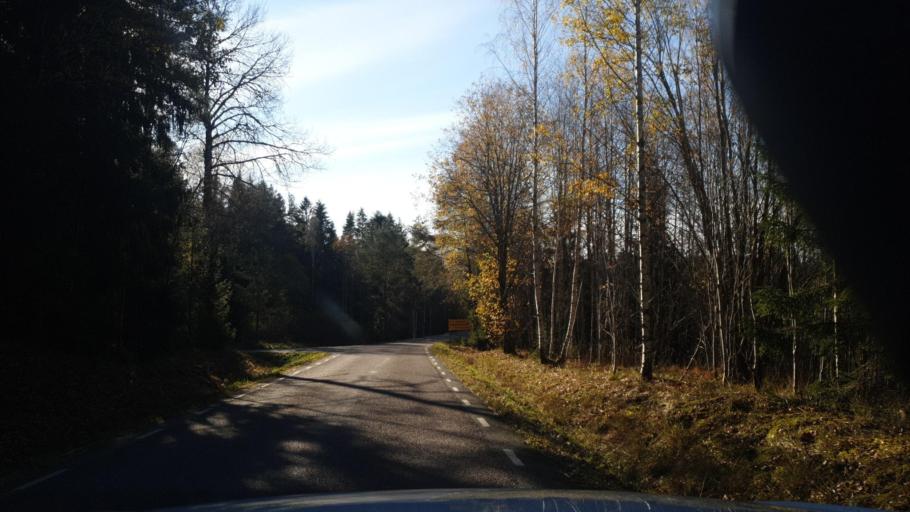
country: SE
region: Vaermland
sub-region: Karlstads Kommun
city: Edsvalla
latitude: 59.4973
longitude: 13.1061
